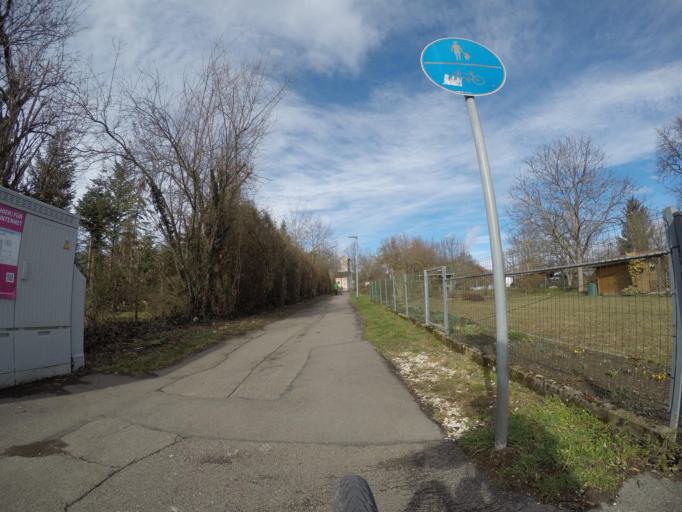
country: DE
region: Baden-Wuerttemberg
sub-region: Tuebingen Region
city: Reutlingen
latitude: 48.5104
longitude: 9.1990
